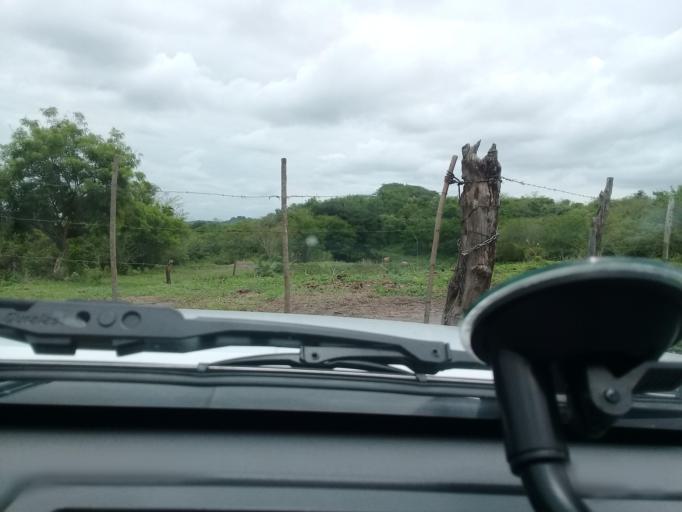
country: MX
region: Veracruz
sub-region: Paso de Ovejas
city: El Hatito
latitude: 19.2750
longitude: -96.3996
